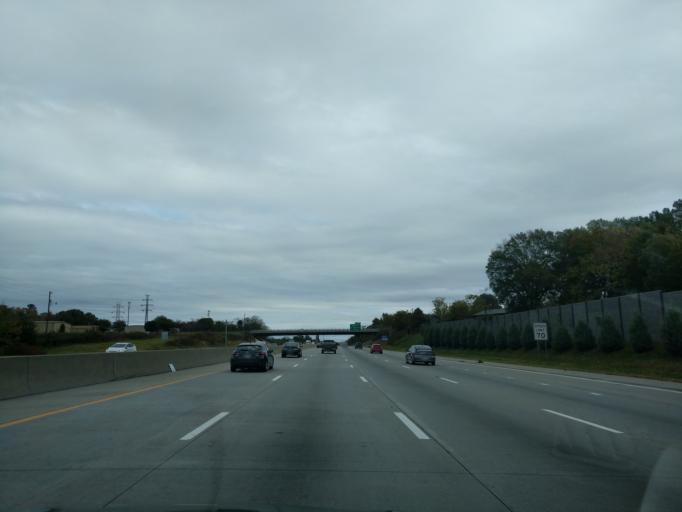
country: US
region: North Carolina
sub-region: Rowan County
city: Salisbury
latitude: 35.6619
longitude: -80.4519
